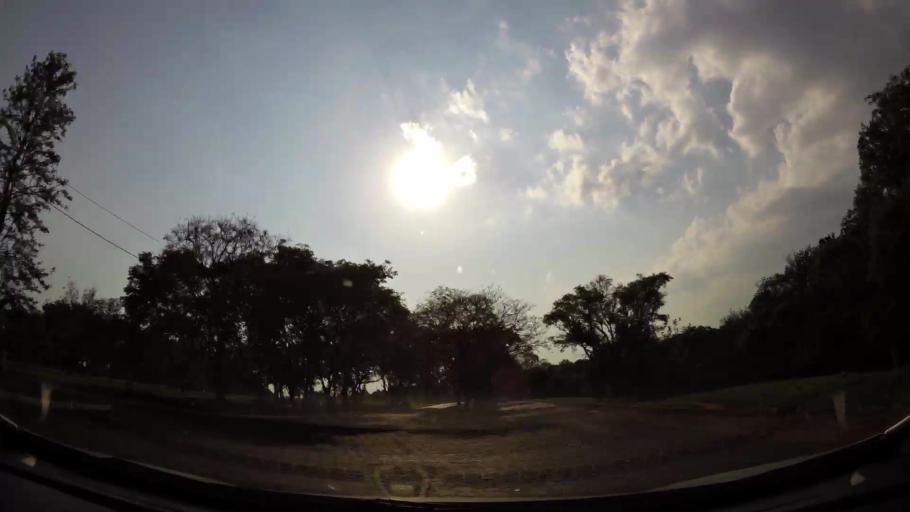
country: PY
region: Alto Parana
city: Presidente Franco
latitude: -25.5239
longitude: -54.6316
